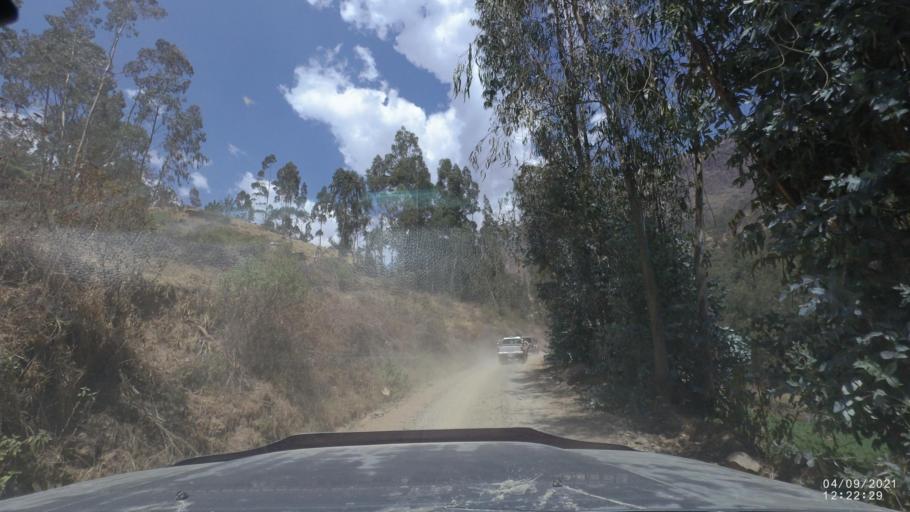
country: BO
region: Cochabamba
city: Colchani
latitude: -17.2391
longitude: -66.5257
